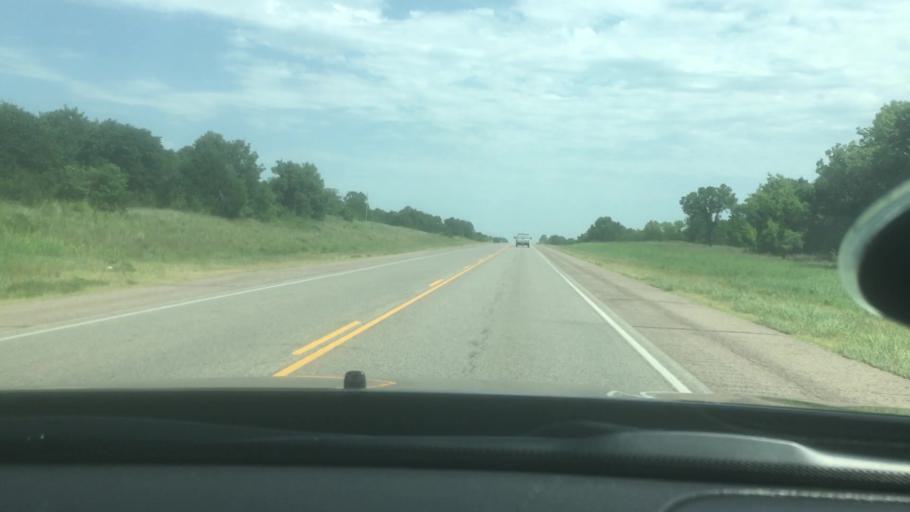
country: US
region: Oklahoma
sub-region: Seminole County
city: Konawa
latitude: 35.0174
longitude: -96.9314
